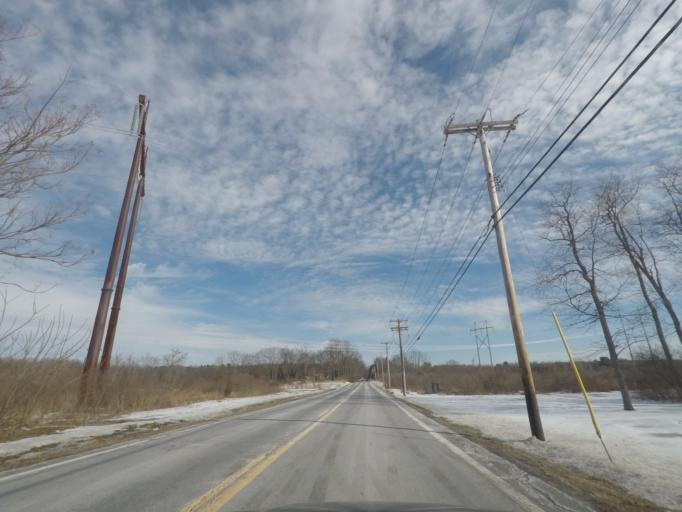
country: US
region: New York
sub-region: Albany County
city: Voorheesville
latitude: 42.6533
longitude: -73.9595
